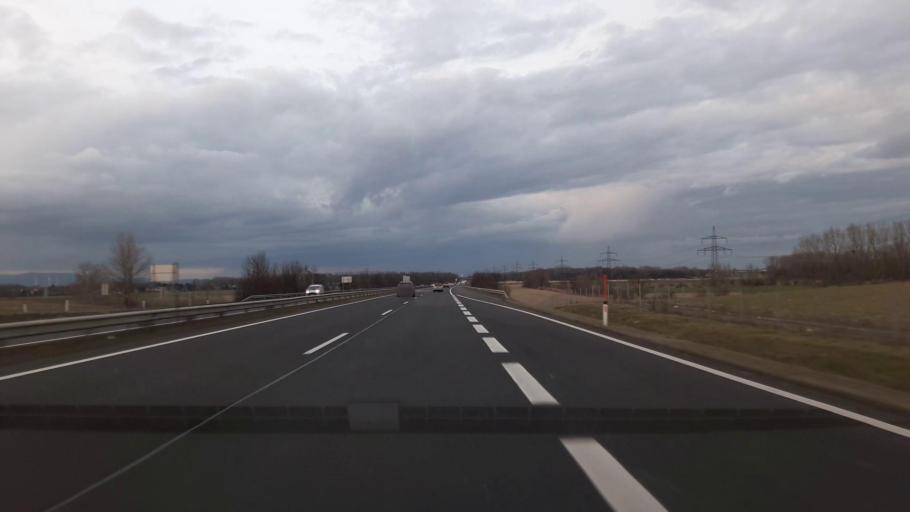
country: AT
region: Burgenland
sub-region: Eisenstadt-Umgebung
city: Hornstein
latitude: 47.8787
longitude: 16.4159
